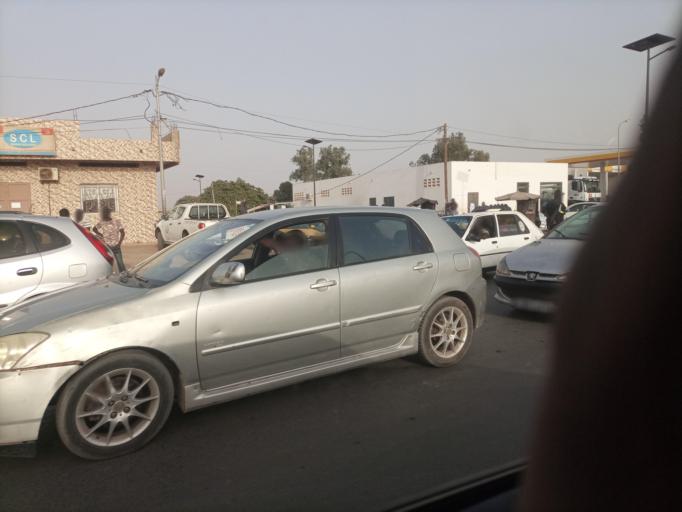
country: SN
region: Thies
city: Nguekhokh
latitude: 14.4440
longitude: -16.9800
